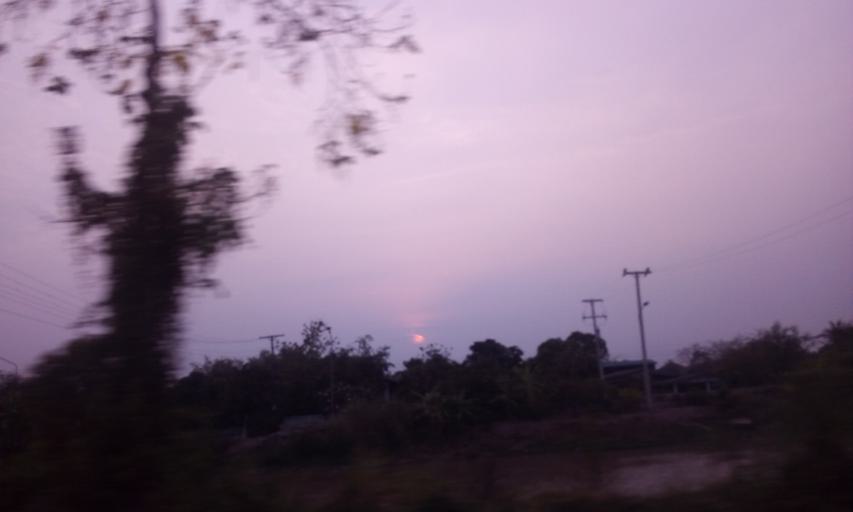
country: TH
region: Pathum Thani
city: Nong Suea
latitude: 14.0551
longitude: 100.8931
